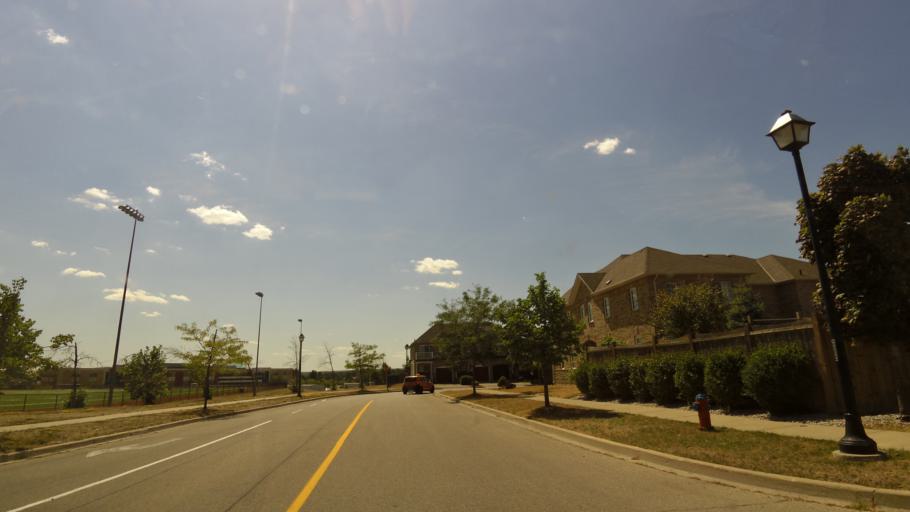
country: CA
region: Ontario
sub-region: Halton
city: Milton
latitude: 43.6536
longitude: -79.9082
